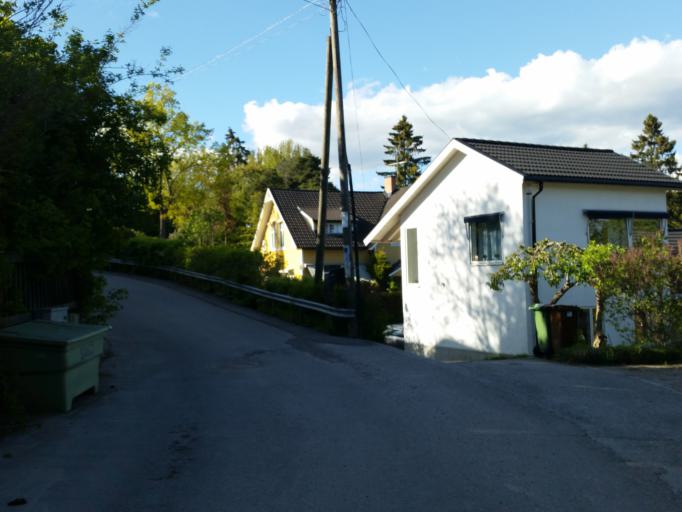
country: SE
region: Stockholm
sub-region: Sundbybergs Kommun
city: Sundbyberg
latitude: 59.3722
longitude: 17.9610
